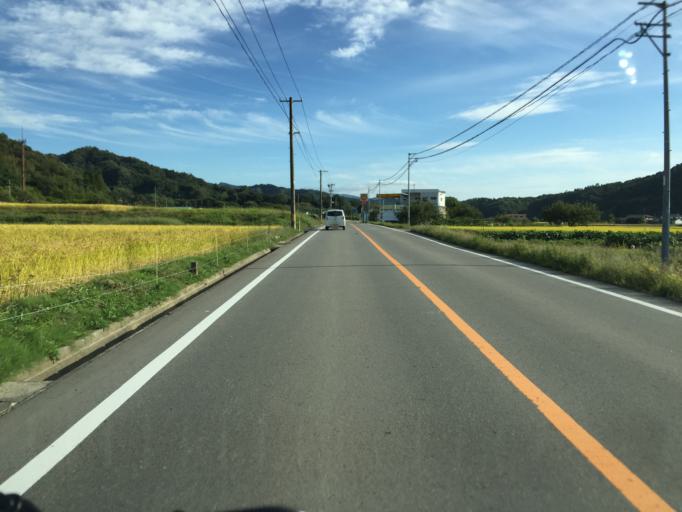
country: JP
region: Fukushima
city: Yanagawamachi-saiwaicho
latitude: 37.8099
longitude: 140.6190
